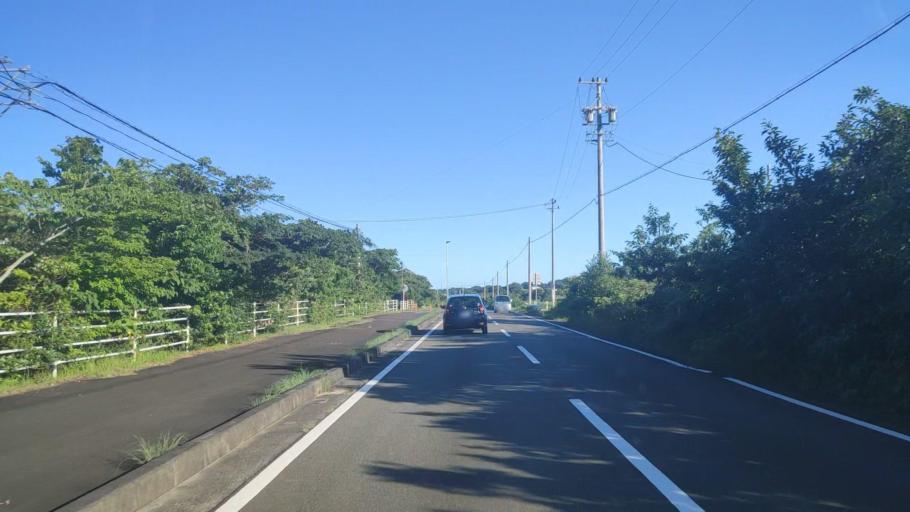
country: JP
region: Mie
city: Toba
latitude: 34.3264
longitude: 136.8748
